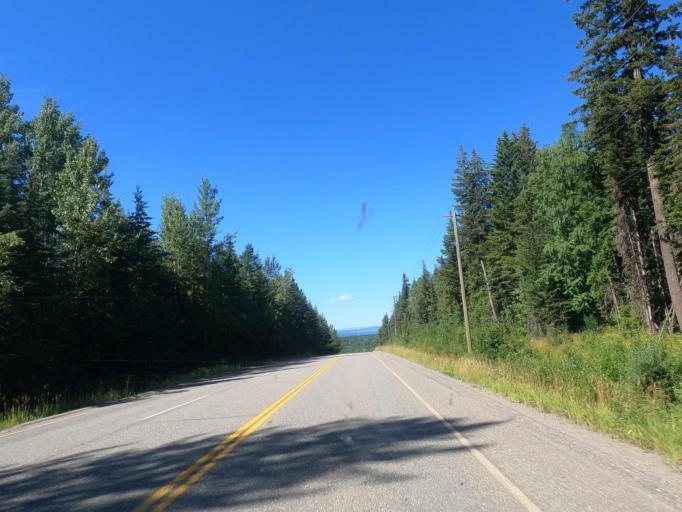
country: CA
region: British Columbia
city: Quesnel
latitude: 53.0244
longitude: -122.3496
